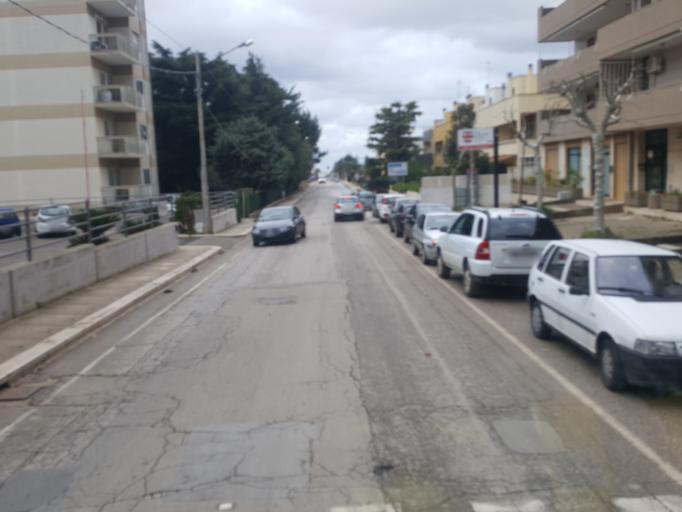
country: IT
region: Apulia
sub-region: Provincia di Bari
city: Turi
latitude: 40.9192
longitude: 17.0144
